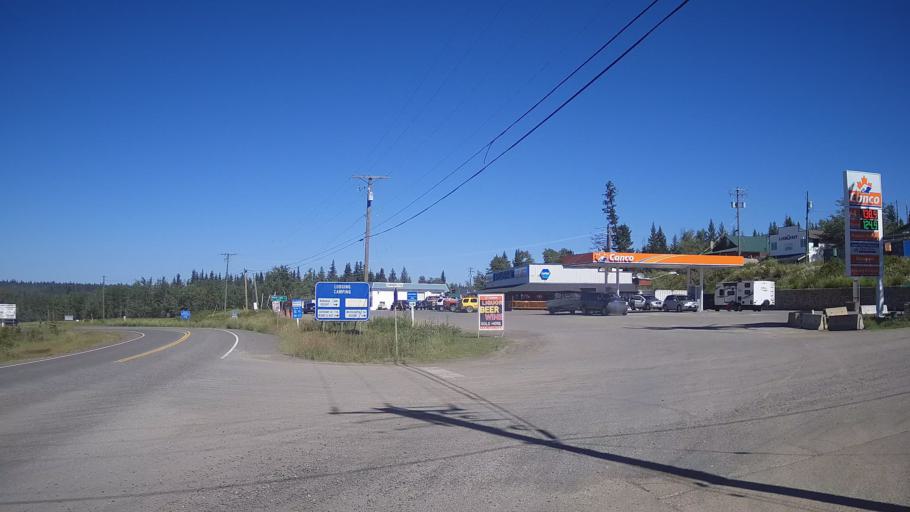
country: CA
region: British Columbia
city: Cache Creek
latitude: 51.5458
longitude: -120.9137
